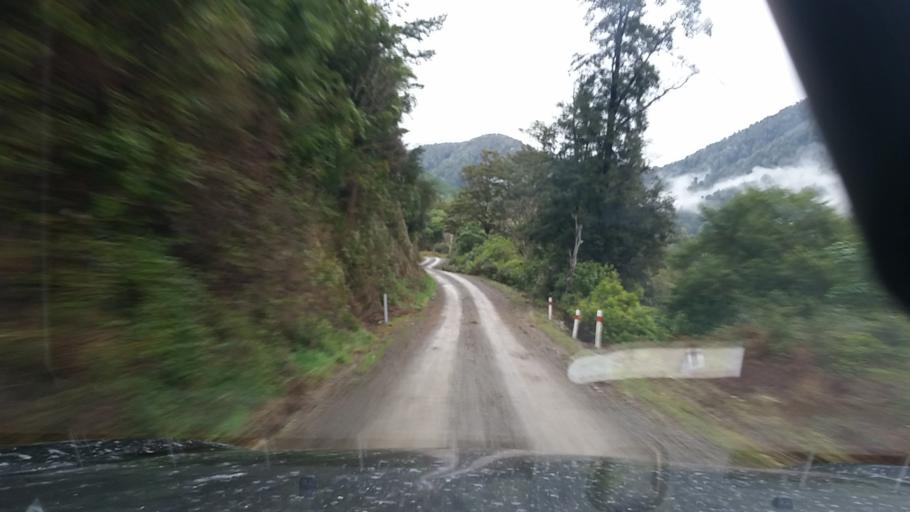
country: NZ
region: Nelson
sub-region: Nelson City
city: Nelson
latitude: -41.3593
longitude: 173.6195
